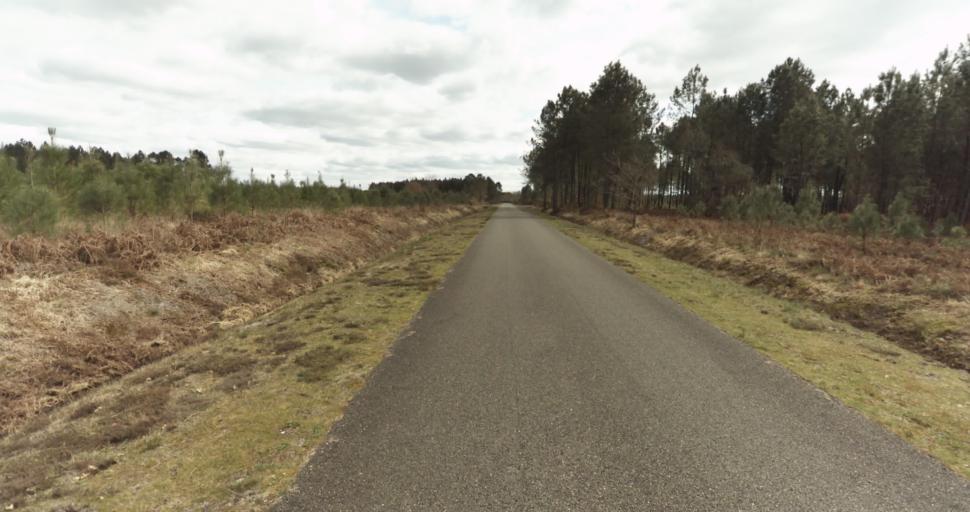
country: FR
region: Aquitaine
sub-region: Departement des Landes
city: Roquefort
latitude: 44.1054
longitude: -0.4407
